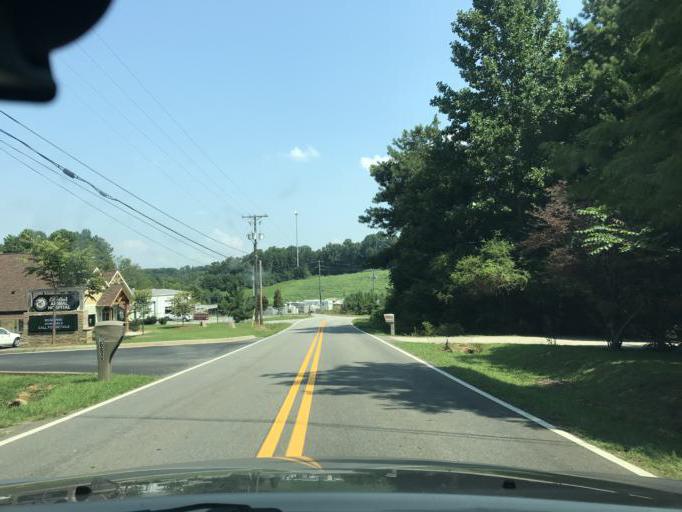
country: US
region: Georgia
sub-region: Hall County
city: Flowery Branch
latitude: 34.2491
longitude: -83.9981
